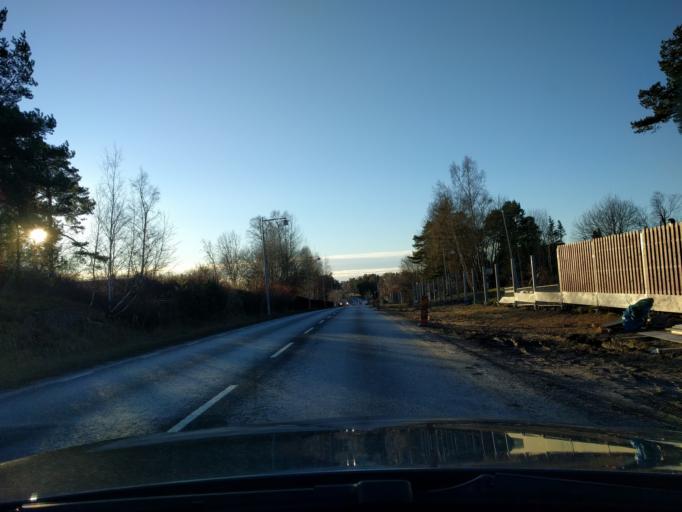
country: SE
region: Stockholm
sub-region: Vallentuna Kommun
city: Vallentuna
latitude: 59.5013
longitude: 18.0655
